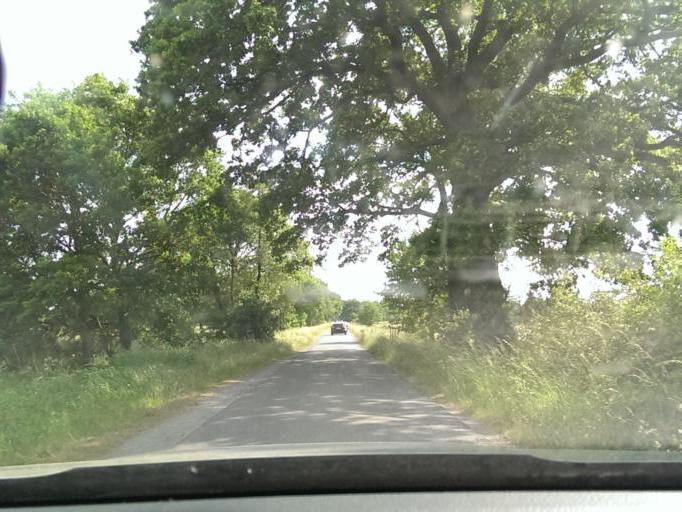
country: DE
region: Lower Saxony
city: Lindwedel
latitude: 52.5450
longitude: 9.6712
